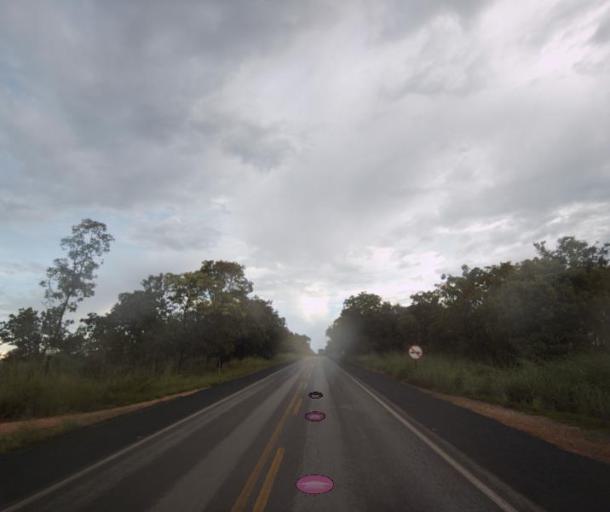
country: BR
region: Goias
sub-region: Porangatu
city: Porangatu
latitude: -13.9008
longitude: -49.0608
